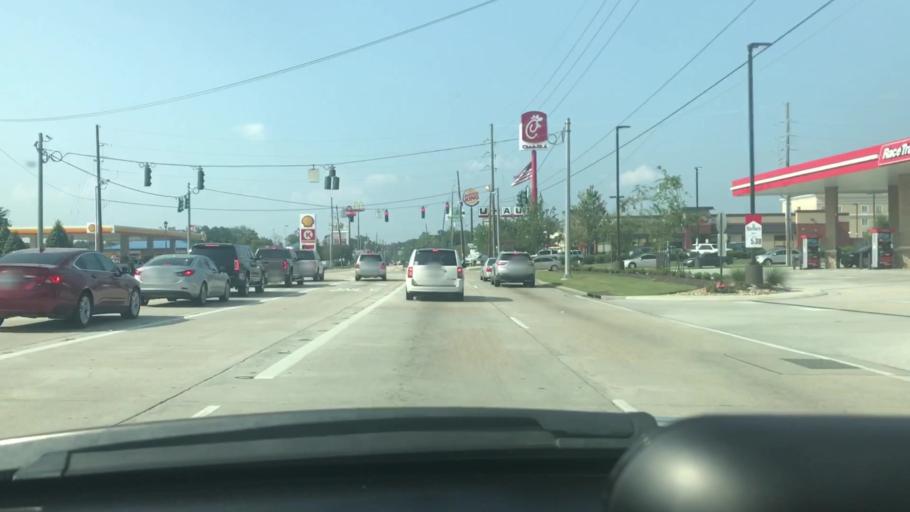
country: US
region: Louisiana
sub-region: Tangipahoa Parish
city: Hammond
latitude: 30.4809
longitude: -90.4569
